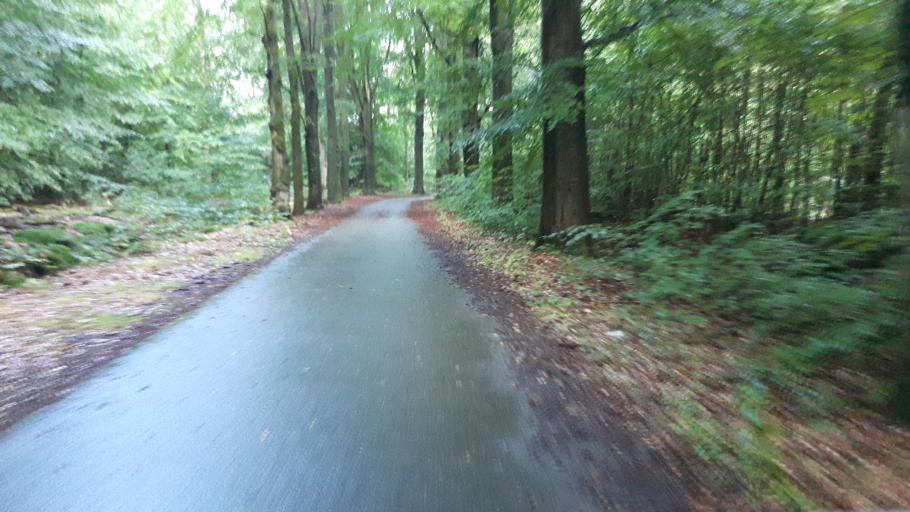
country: NL
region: Friesland
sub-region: Gemeente Smallingerland
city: Drachten
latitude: 53.0639
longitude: 6.1229
